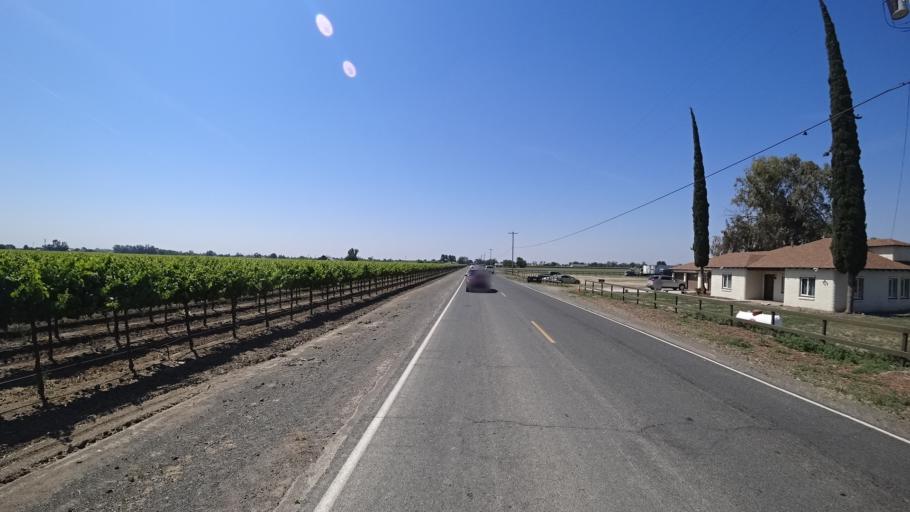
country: US
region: California
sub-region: Fresno County
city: Riverdale
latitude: 36.3704
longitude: -119.8513
